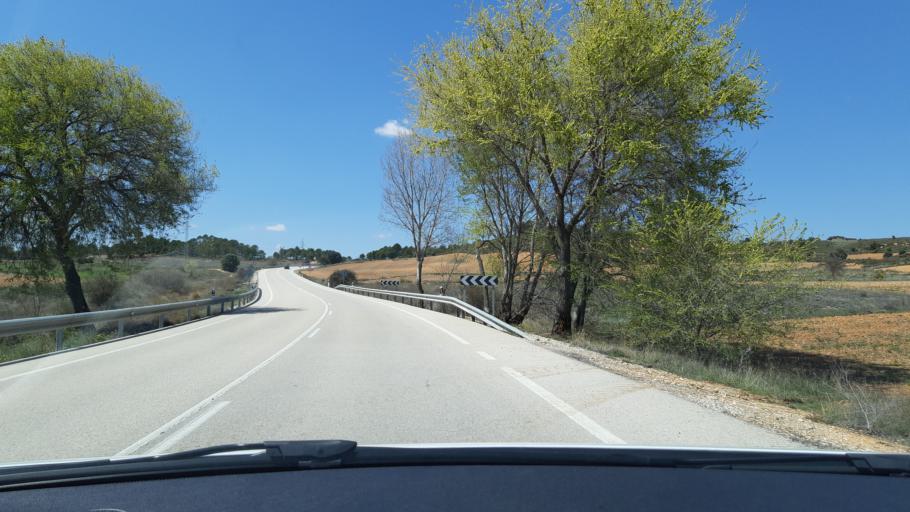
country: ES
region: Castille-La Mancha
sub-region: Provincia de Guadalajara
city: Cifuentes
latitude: 40.7985
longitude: -2.6558
